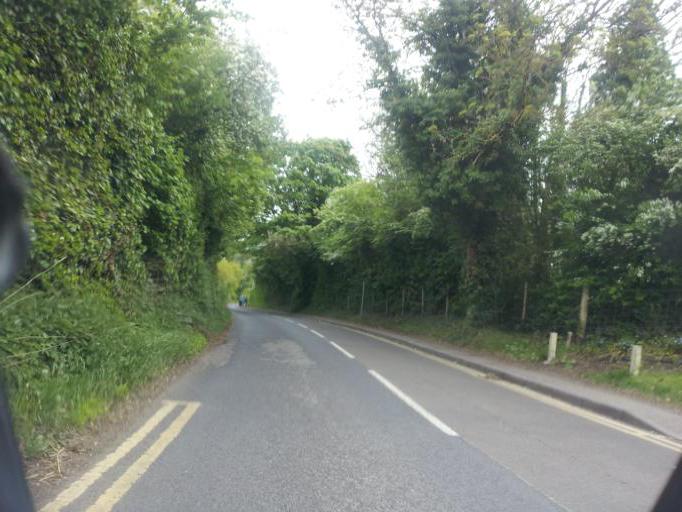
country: GB
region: England
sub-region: Kent
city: Faversham
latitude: 51.3248
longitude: 0.8830
